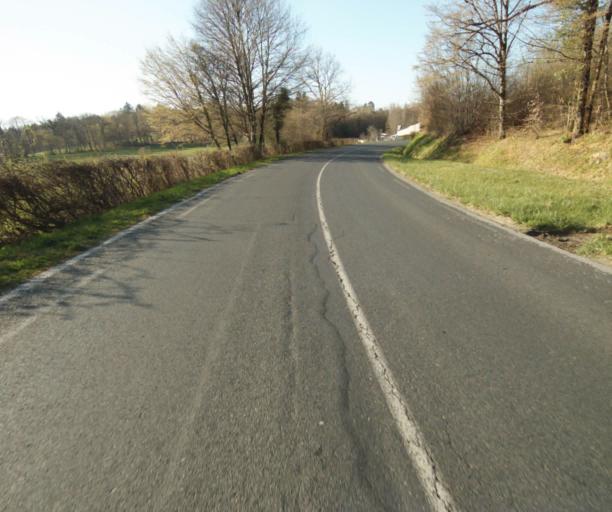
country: FR
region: Limousin
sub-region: Departement de la Correze
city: Saint-Clement
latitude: 45.3323
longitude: 1.6800
